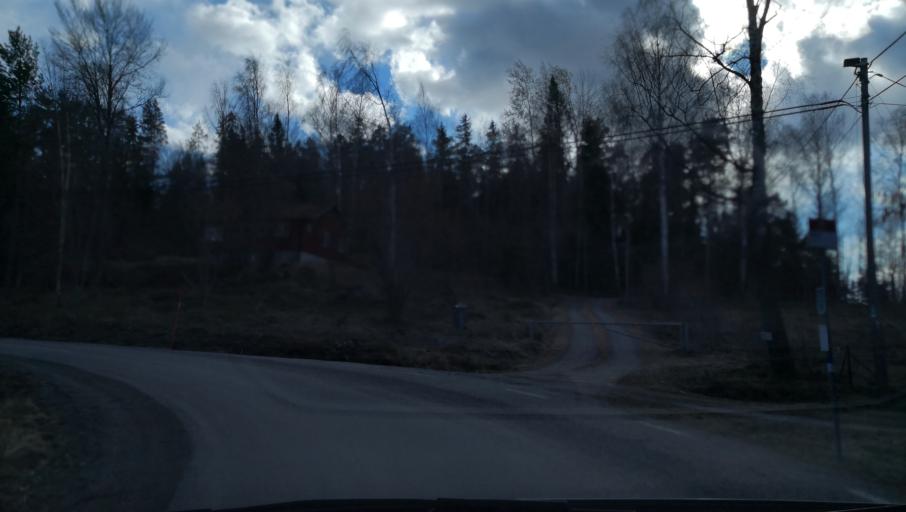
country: SE
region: Stockholm
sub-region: Varmdo Kommun
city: Mortnas
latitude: 59.3859
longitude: 18.4531
